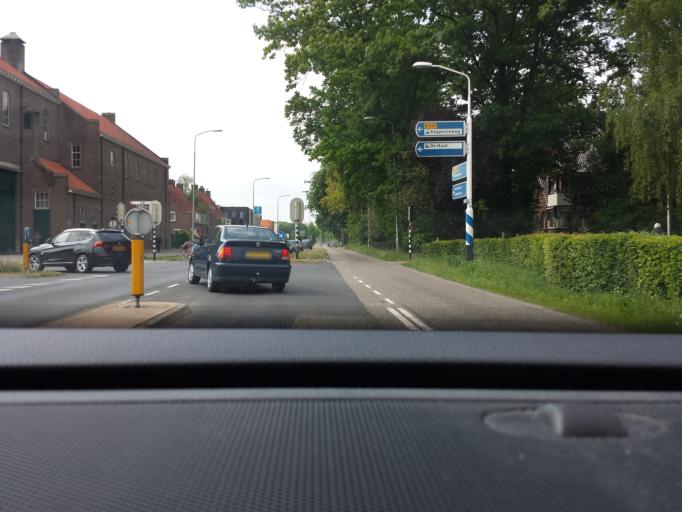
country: NL
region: Gelderland
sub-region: Gemeente Doetinchem
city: Doetinchem
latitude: 51.9722
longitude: 6.2764
